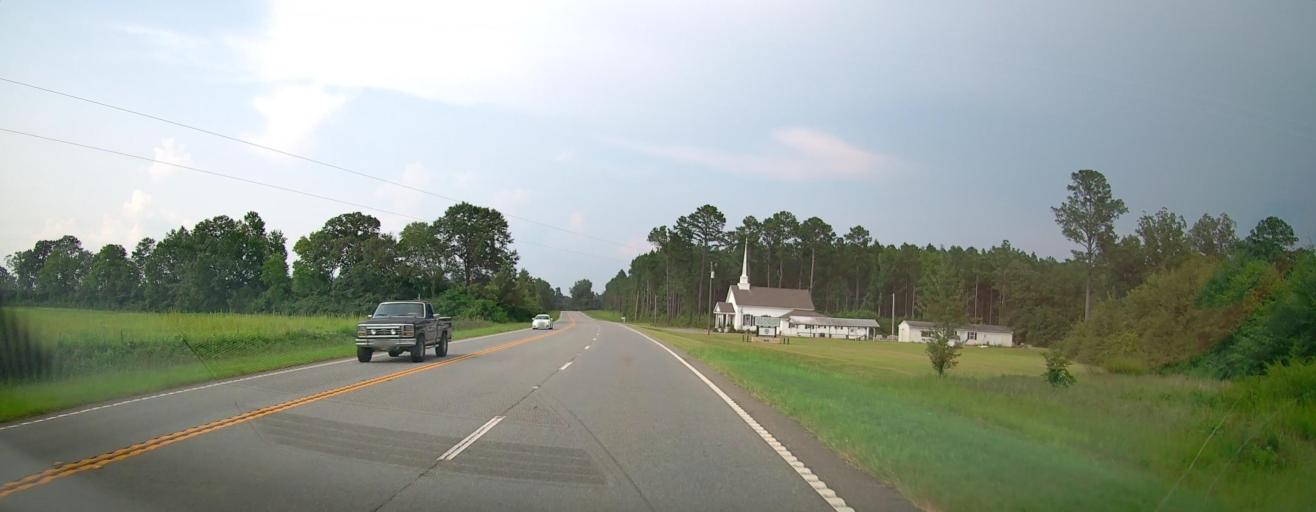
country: US
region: Georgia
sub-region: Twiggs County
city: Jeffersonville
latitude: 32.5676
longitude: -83.4093
